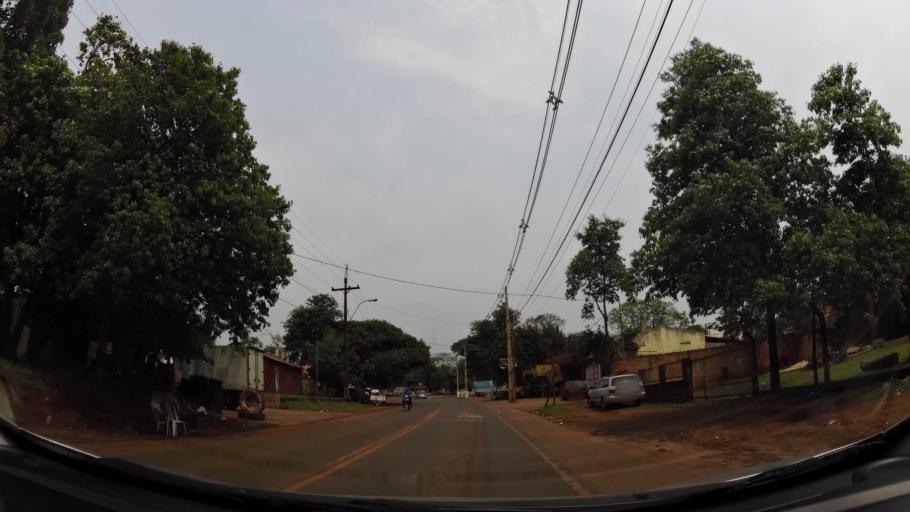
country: PY
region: Alto Parana
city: Presidente Franco
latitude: -25.5528
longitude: -54.6388
